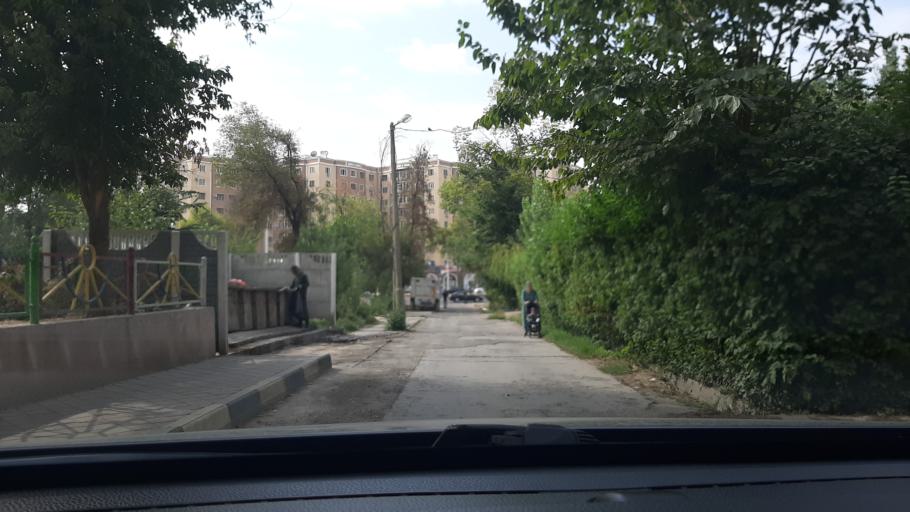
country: TJ
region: Dushanbe
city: Dushanbe
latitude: 38.5854
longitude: 68.7522
